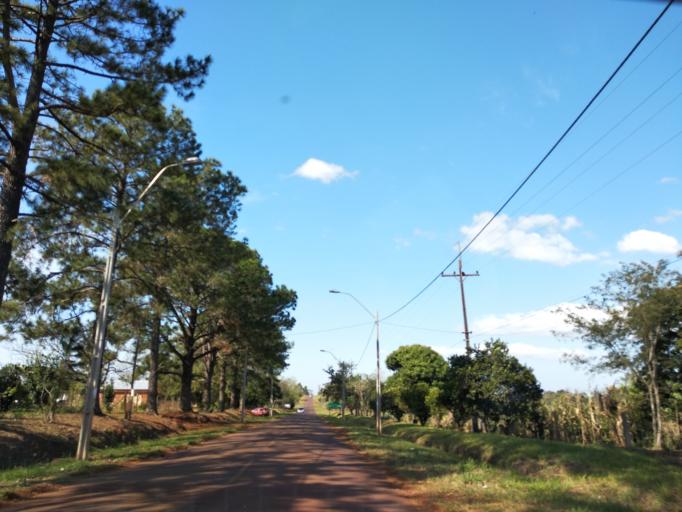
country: PY
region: Itapua
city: Hohenau
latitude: -27.0617
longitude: -55.7299
